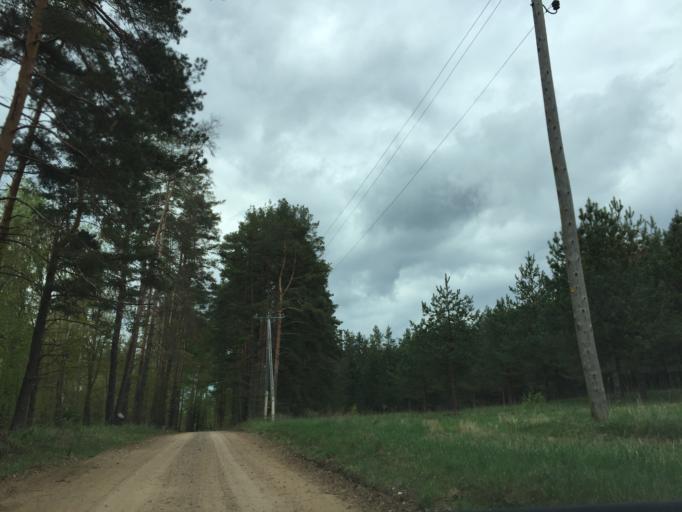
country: LV
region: Kekava
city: Kekava
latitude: 56.7946
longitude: 24.3086
